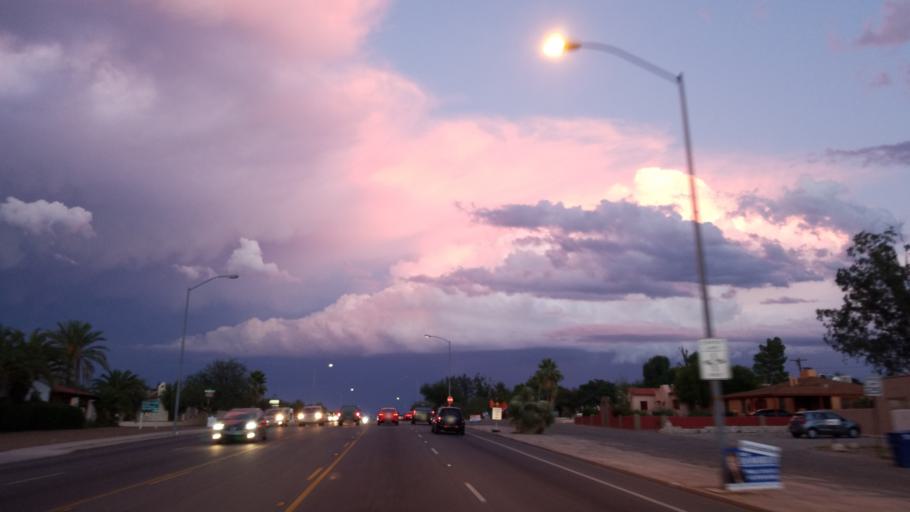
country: US
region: Arizona
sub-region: Pima County
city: Tucson
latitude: 32.2502
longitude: -110.9419
